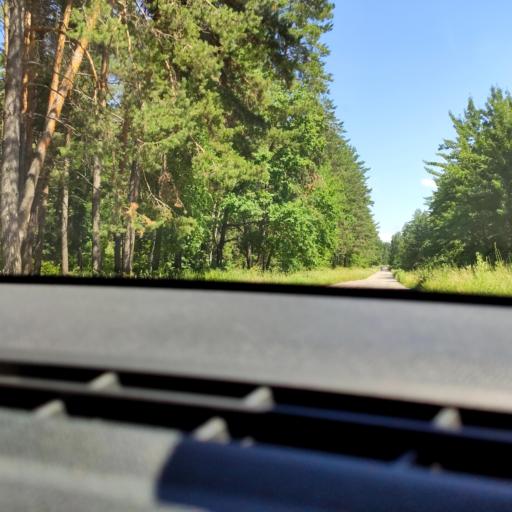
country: RU
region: Samara
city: Podstepki
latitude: 53.5661
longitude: 49.0224
